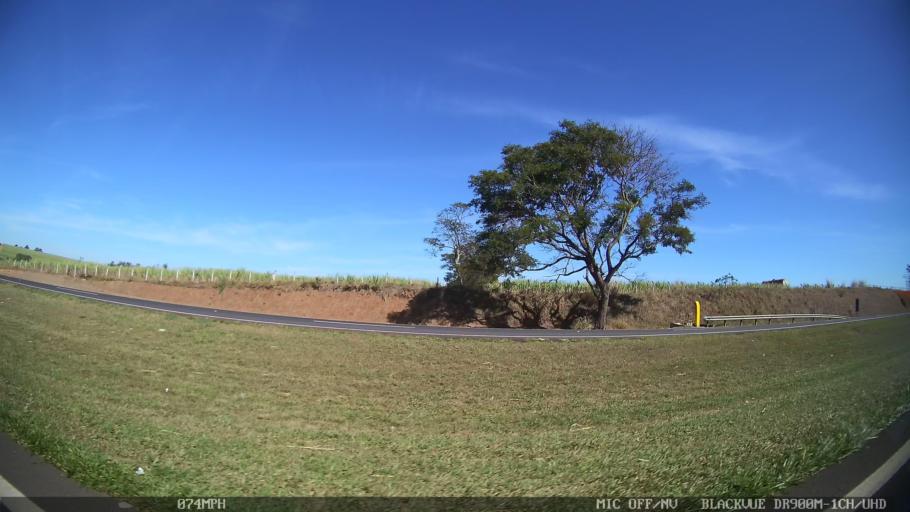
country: BR
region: Sao Paulo
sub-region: Santa Rita Do Passa Quatro
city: Santa Rita do Passa Quatro
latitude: -21.7667
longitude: -47.5501
